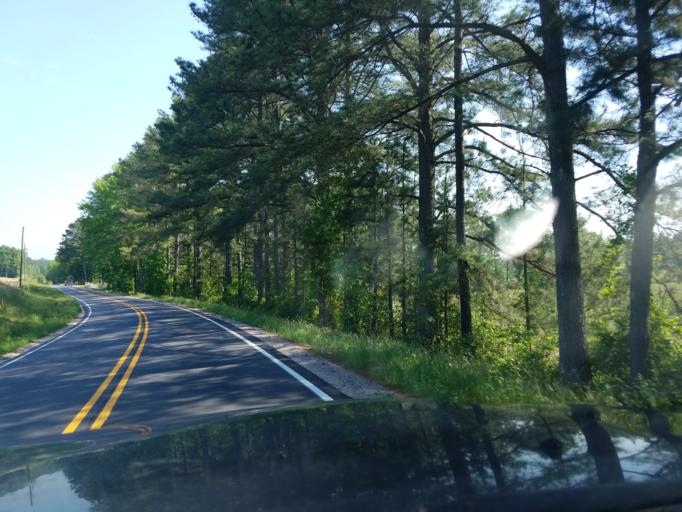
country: US
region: North Carolina
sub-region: Vance County
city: Henderson
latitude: 36.3739
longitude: -78.4462
